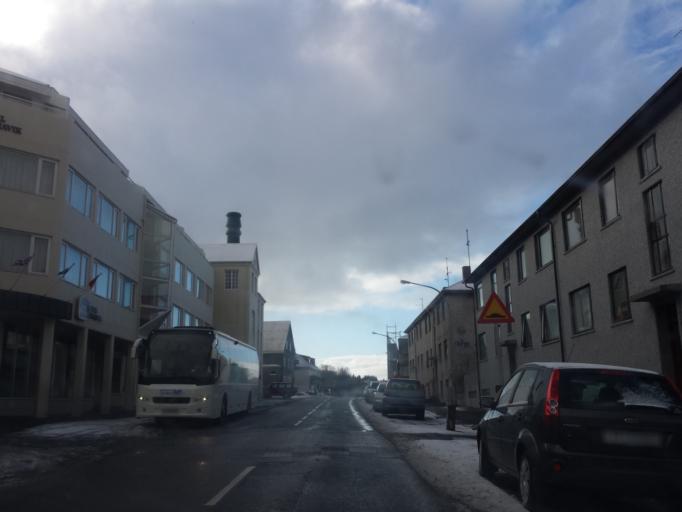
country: IS
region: Capital Region
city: Reykjavik
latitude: 64.1408
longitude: -21.9149
